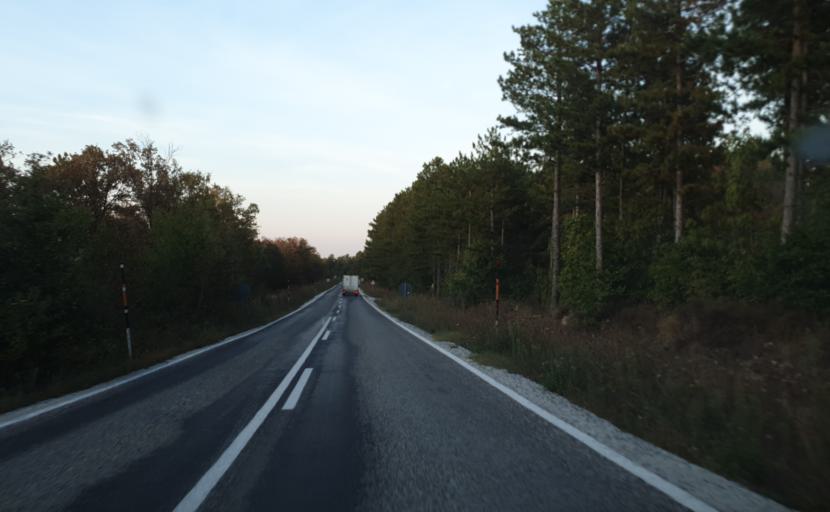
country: TR
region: Kirklareli
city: Igneada
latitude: 41.8639
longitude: 27.8839
